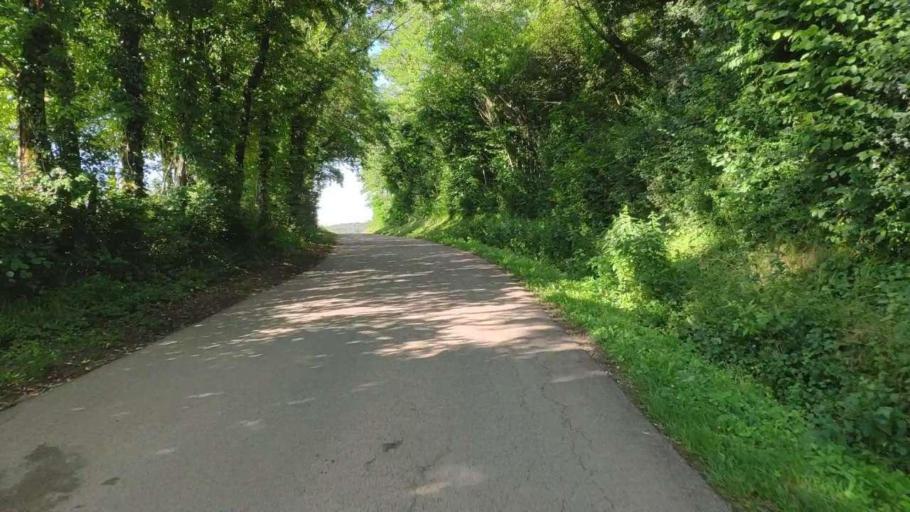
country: FR
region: Franche-Comte
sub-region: Departement du Jura
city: Bletterans
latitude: 46.7541
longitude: 5.5257
